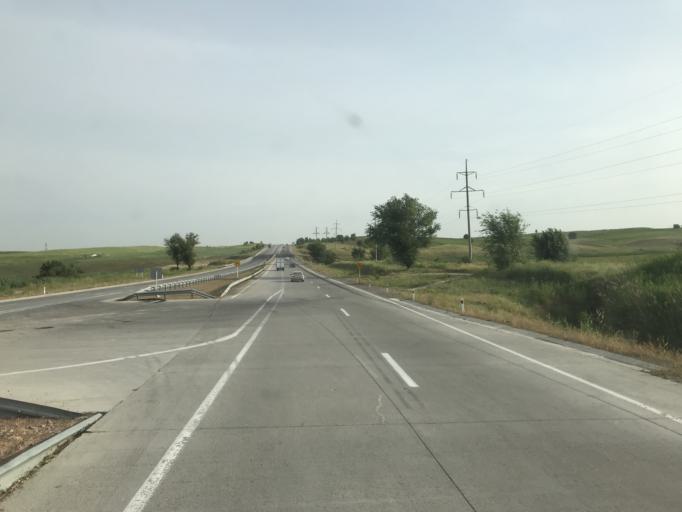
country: KZ
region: Ongtustik Qazaqstan
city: Qazyqurt
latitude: 41.5957
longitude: 69.4060
